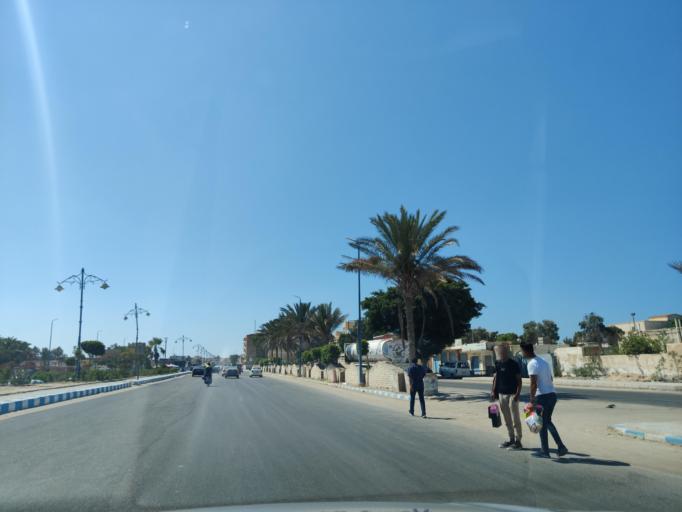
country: EG
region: Muhafazat Matruh
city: Mersa Matruh
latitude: 31.3396
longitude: 27.2498
